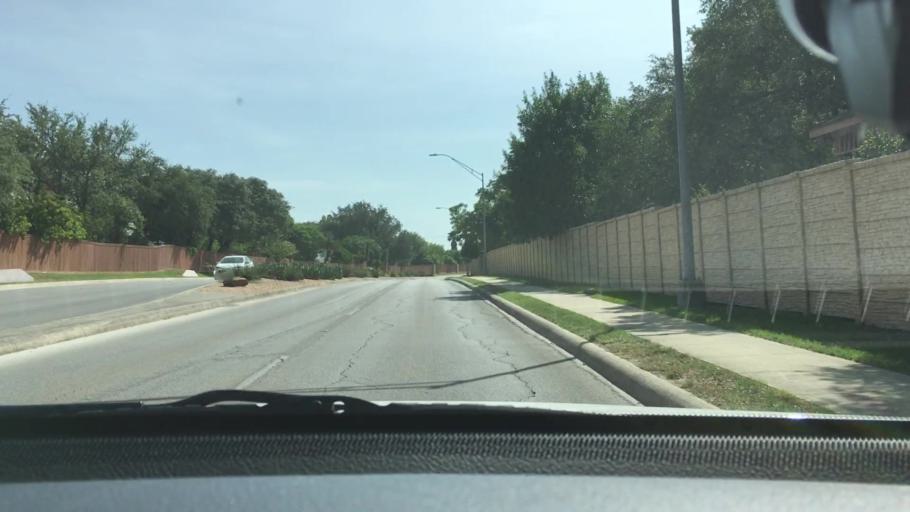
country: US
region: Texas
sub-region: Bexar County
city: Live Oak
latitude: 29.5885
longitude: -98.3995
